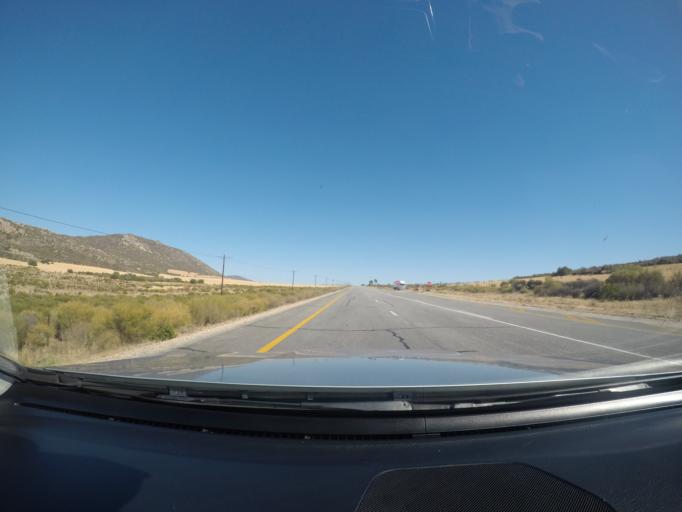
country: ZA
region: Western Cape
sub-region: West Coast District Municipality
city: Clanwilliam
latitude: -32.2920
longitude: 18.8979
